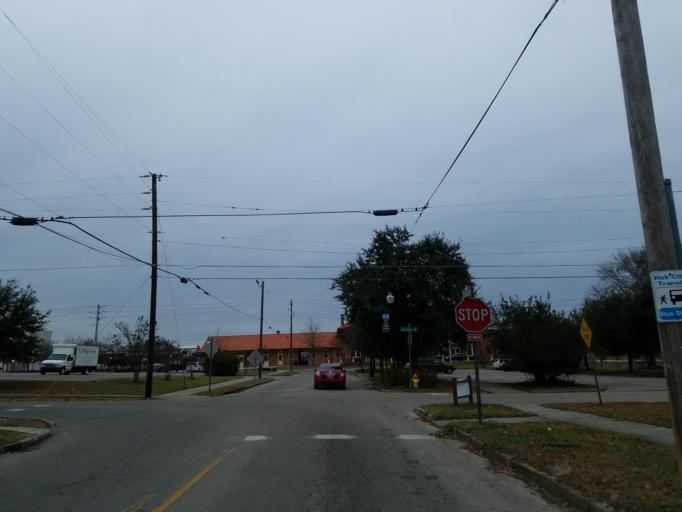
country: US
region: Mississippi
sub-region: Forrest County
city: Hattiesburg
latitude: 31.3263
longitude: -89.2856
